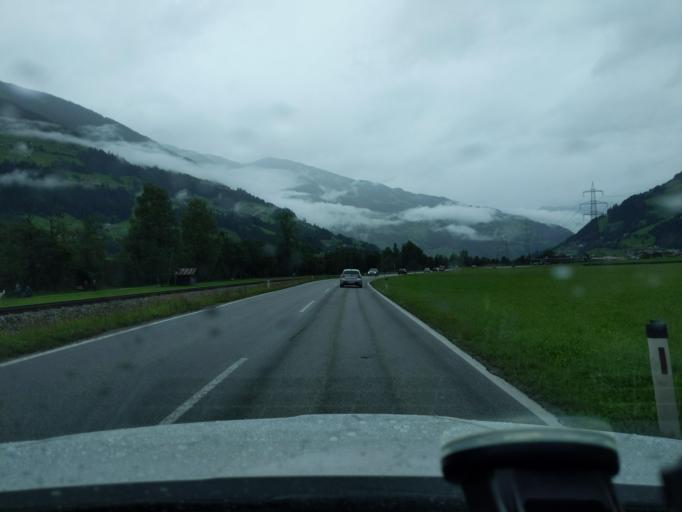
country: AT
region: Tyrol
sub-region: Politischer Bezirk Schwaz
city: Schwendau
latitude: 47.1844
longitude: 11.8664
